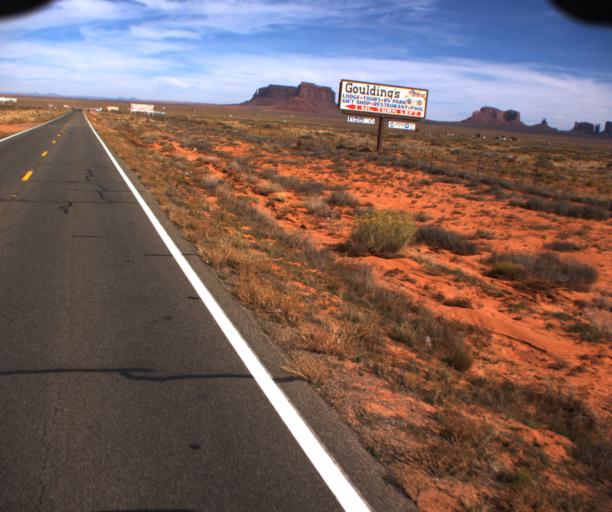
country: US
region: Arizona
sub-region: Navajo County
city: Kayenta
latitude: 36.9910
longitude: -110.1785
